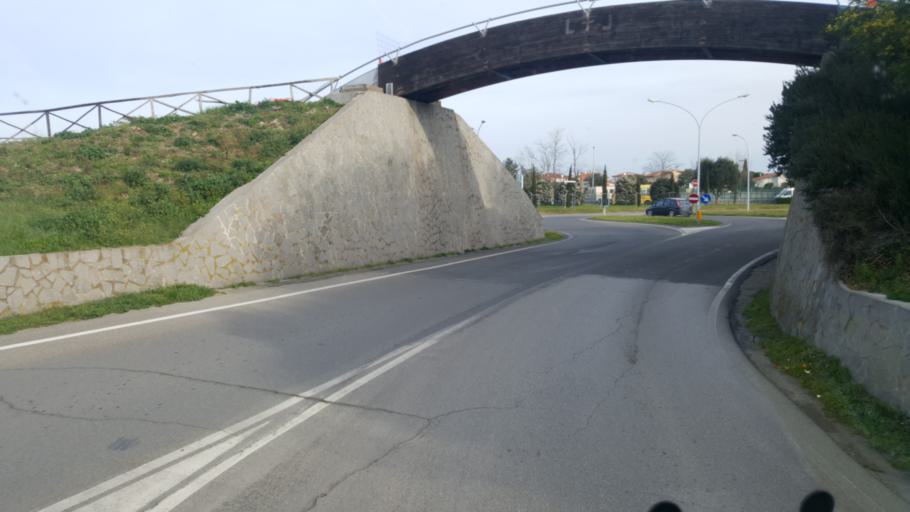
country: IT
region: Latium
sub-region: Provincia di Viterbo
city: Montalto di Castro
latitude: 42.3488
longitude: 11.6123
